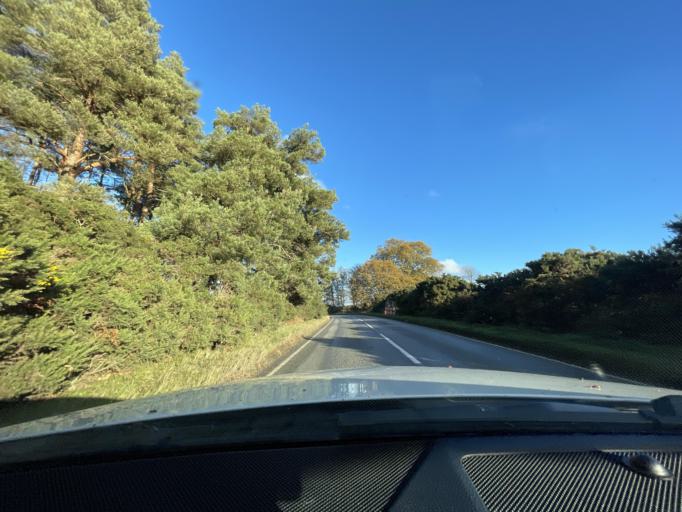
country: GB
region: Scotland
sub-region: Highland
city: Inverness
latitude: 57.3925
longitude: -4.3242
